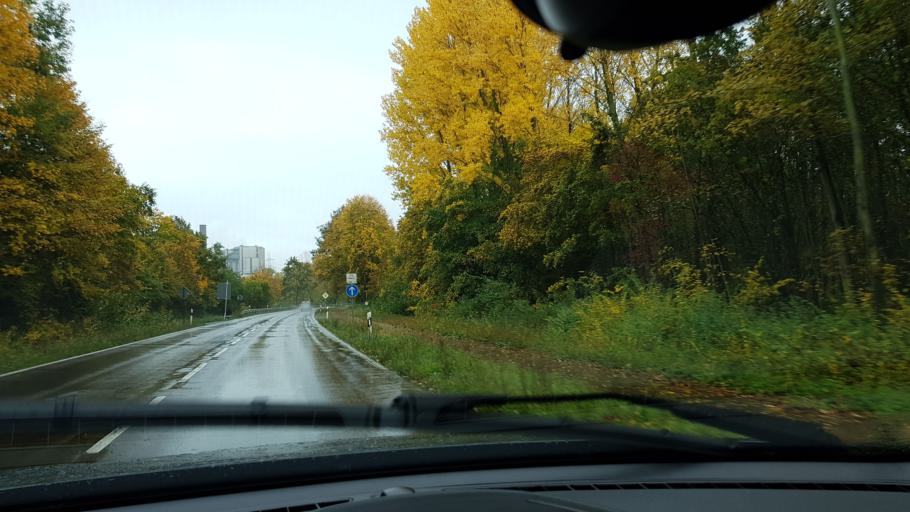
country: DE
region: North Rhine-Westphalia
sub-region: Regierungsbezirk Dusseldorf
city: Grevenbroich
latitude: 51.0459
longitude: 6.5956
